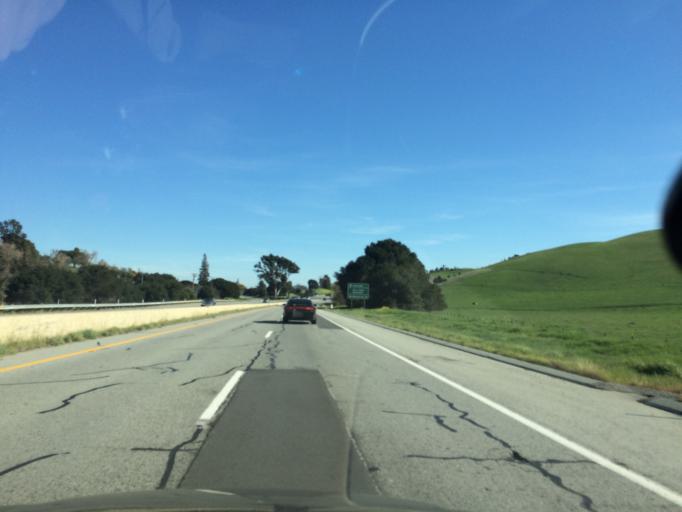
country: US
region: California
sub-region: San Benito County
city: San Juan Bautista
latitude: 36.8468
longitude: -121.5498
